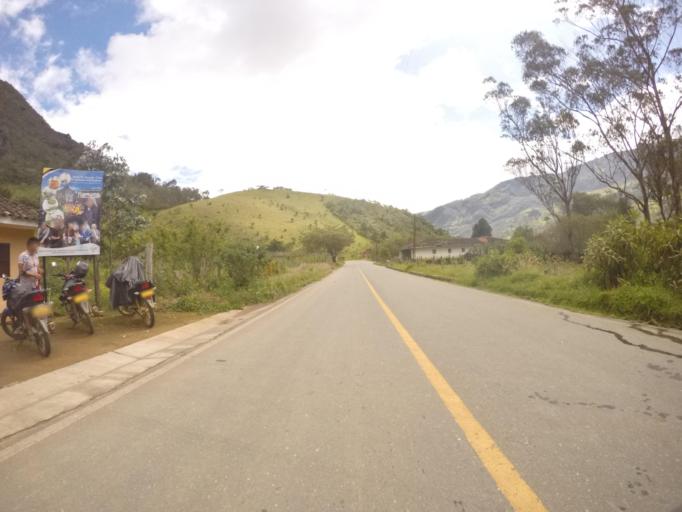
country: CO
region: Cauca
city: Jambalo
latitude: 2.7191
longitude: -76.3246
